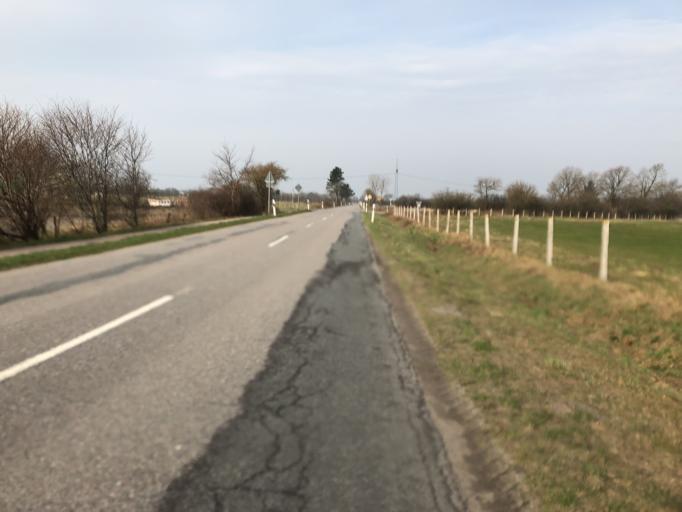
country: DE
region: Schleswig-Holstein
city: Oeversee
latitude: 54.7045
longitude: 9.4223
